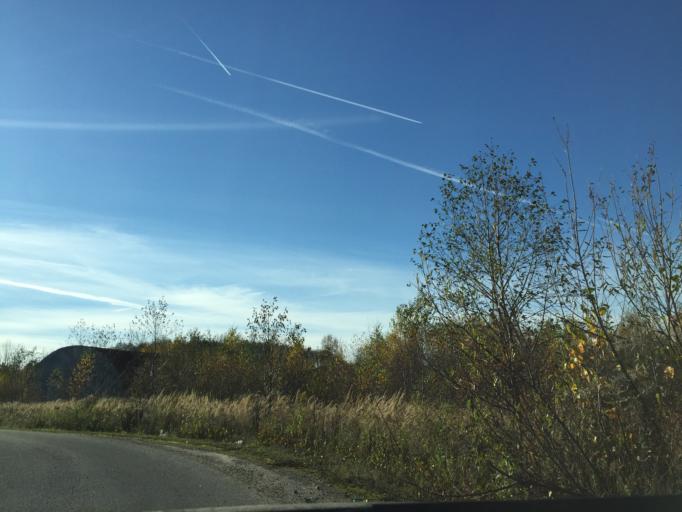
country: LV
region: Aizkraukles Rajons
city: Aizkraukle
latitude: 56.6114
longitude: 25.2594
